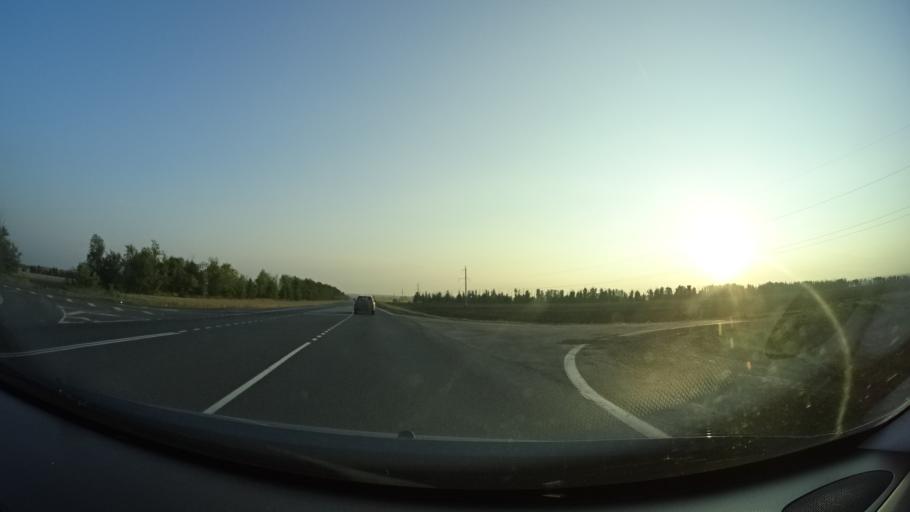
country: RU
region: Samara
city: Sernovodsk
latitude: 53.9576
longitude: 51.4007
